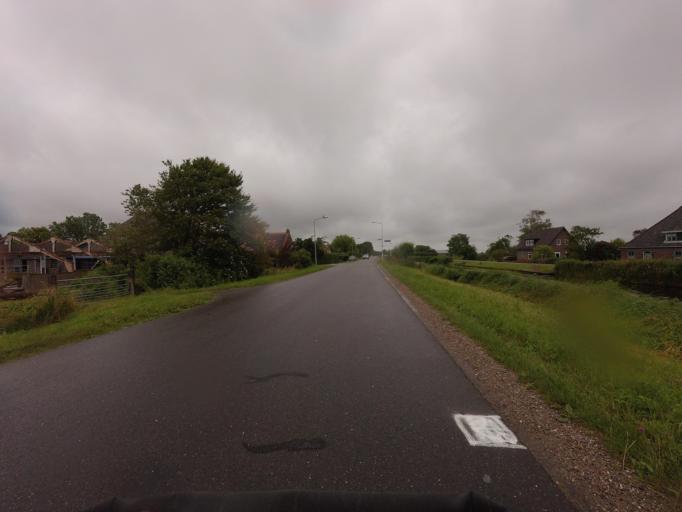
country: NL
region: North Holland
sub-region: Gemeente Opmeer
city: Opmeer
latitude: 52.7366
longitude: 4.9265
